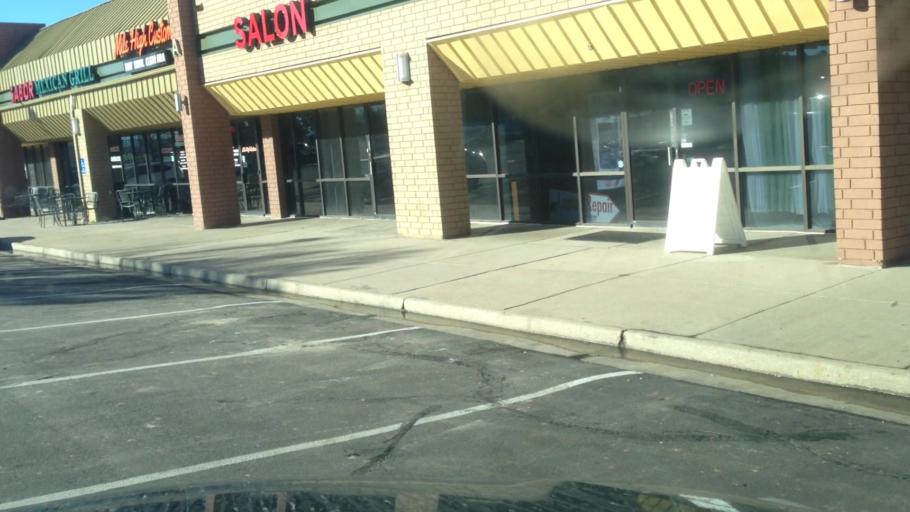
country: US
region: Colorado
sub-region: Arapahoe County
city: Dove Valley
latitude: 39.5955
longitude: -104.8456
